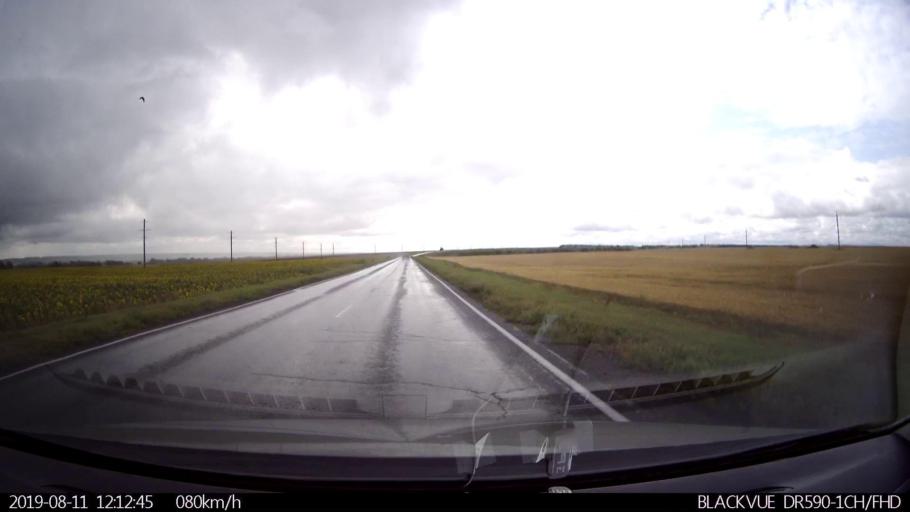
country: RU
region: Ulyanovsk
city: Silikatnyy
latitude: 53.9699
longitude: 47.9955
